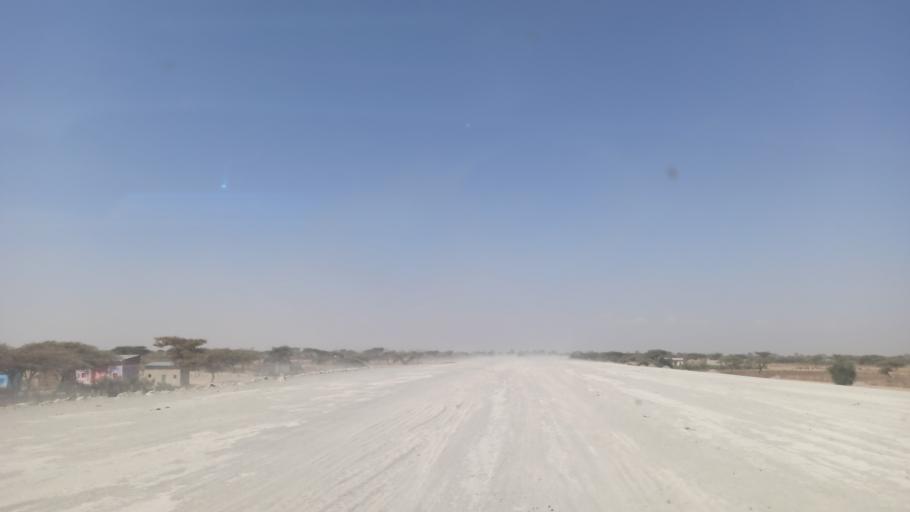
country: ET
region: Oromiya
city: Ziway
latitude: 7.6913
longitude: 38.6583
